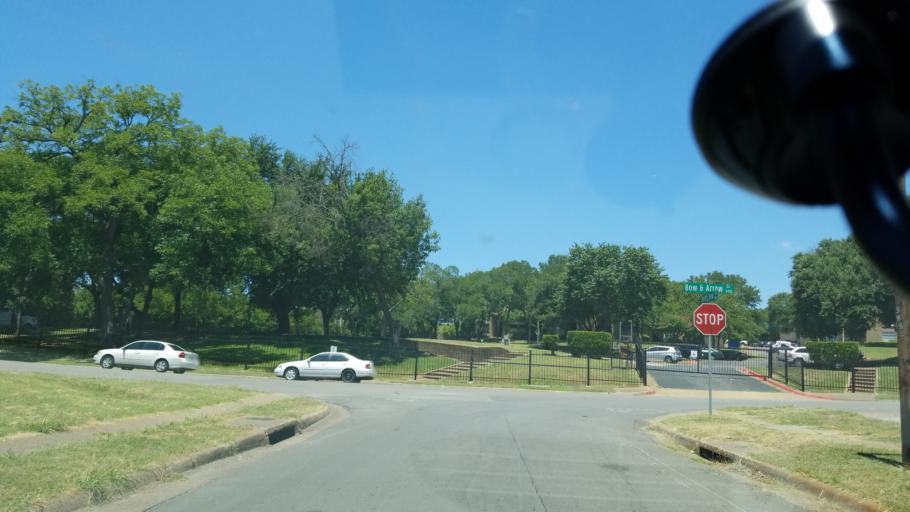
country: US
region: Texas
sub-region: Dallas County
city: Cockrell Hill
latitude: 32.6969
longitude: -96.8347
